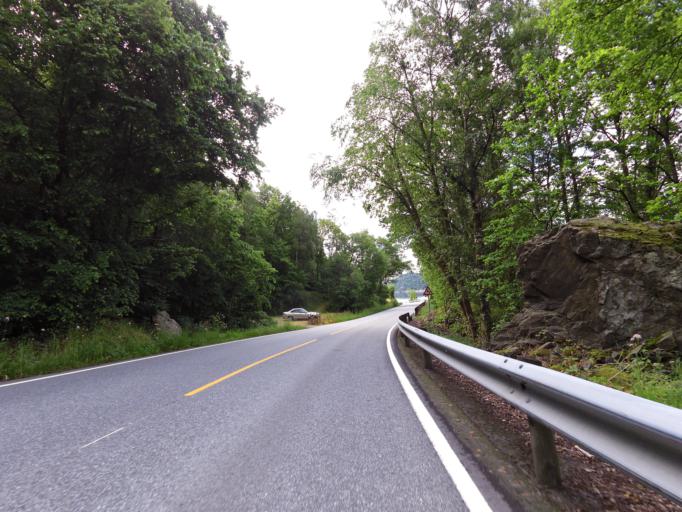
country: NO
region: Vest-Agder
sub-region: Lindesnes
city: Vigeland
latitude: 58.0532
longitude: 7.1830
